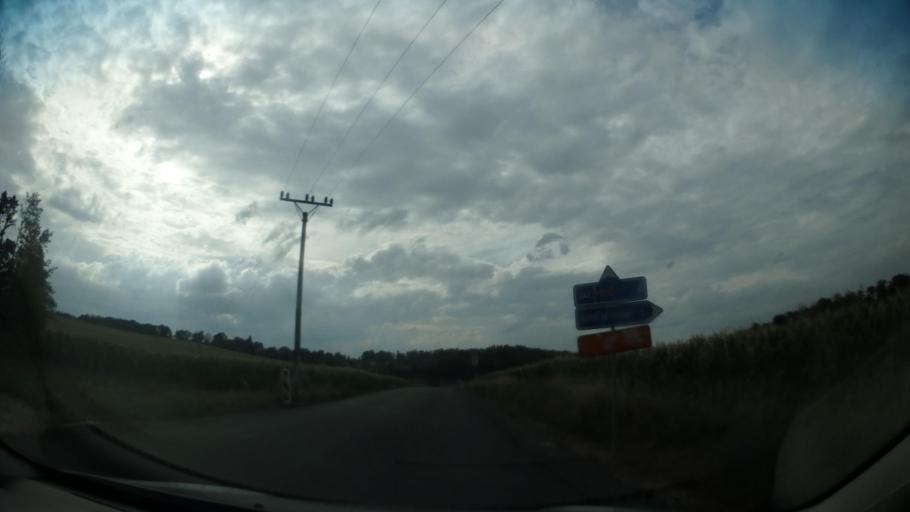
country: CZ
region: Pardubicky
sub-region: Okres Chrudim
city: Sec
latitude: 49.8206
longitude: 15.7029
